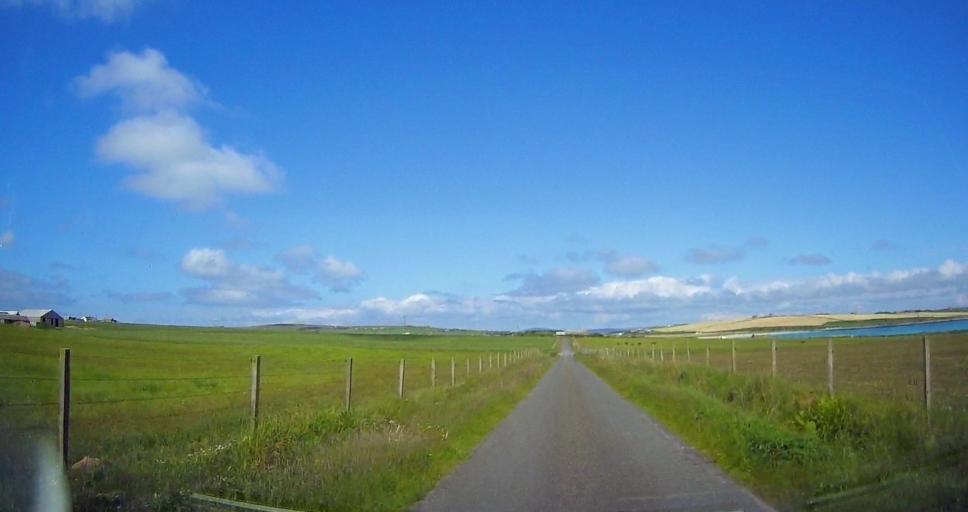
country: GB
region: Scotland
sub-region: Orkney Islands
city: Kirkwall
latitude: 58.8321
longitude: -2.8990
